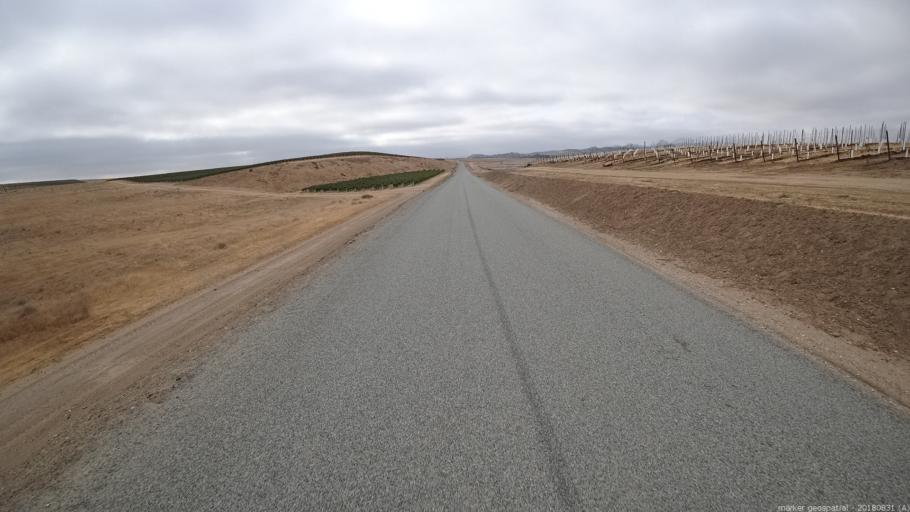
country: US
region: California
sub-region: Monterey County
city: King City
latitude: 36.1652
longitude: -121.1143
